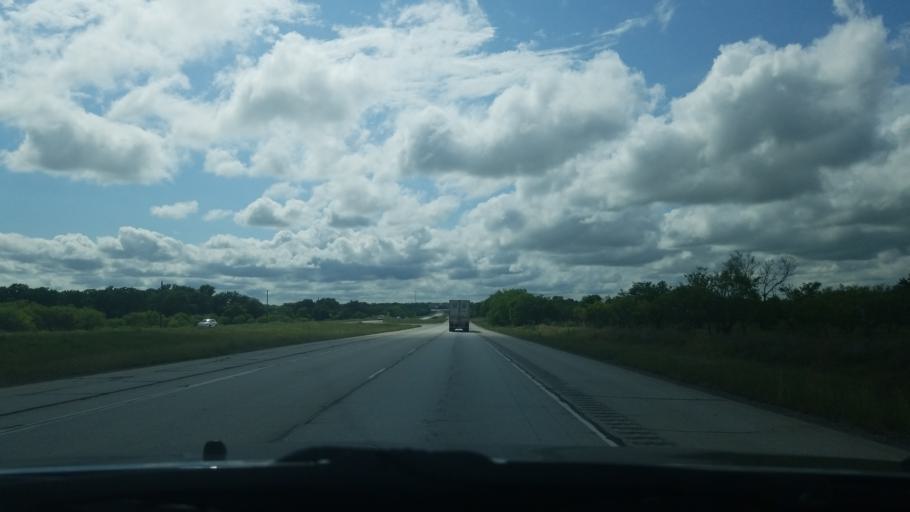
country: US
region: Texas
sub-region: Denton County
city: Ponder
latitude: 33.2471
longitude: -97.3950
